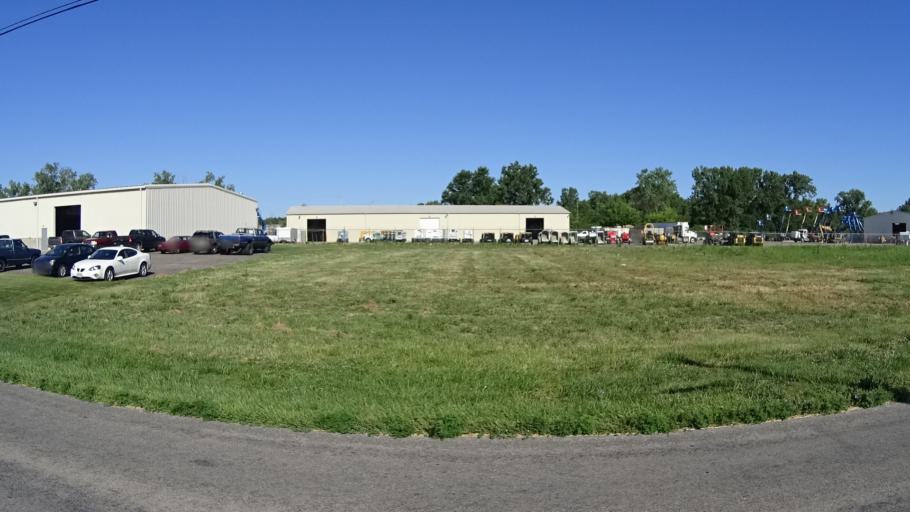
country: US
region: Ohio
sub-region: Erie County
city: Sandusky
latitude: 41.4241
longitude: -82.7341
